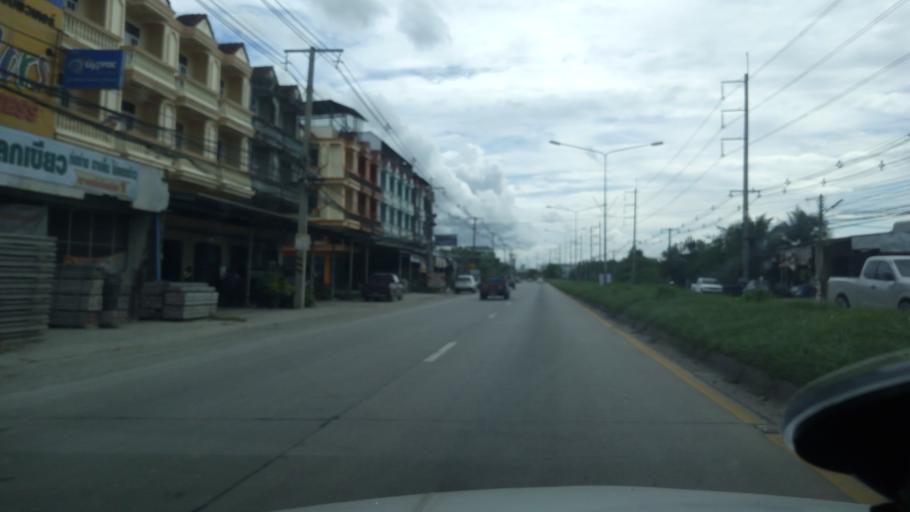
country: TH
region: Chon Buri
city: Phanat Nikhom
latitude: 13.4407
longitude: 101.1470
